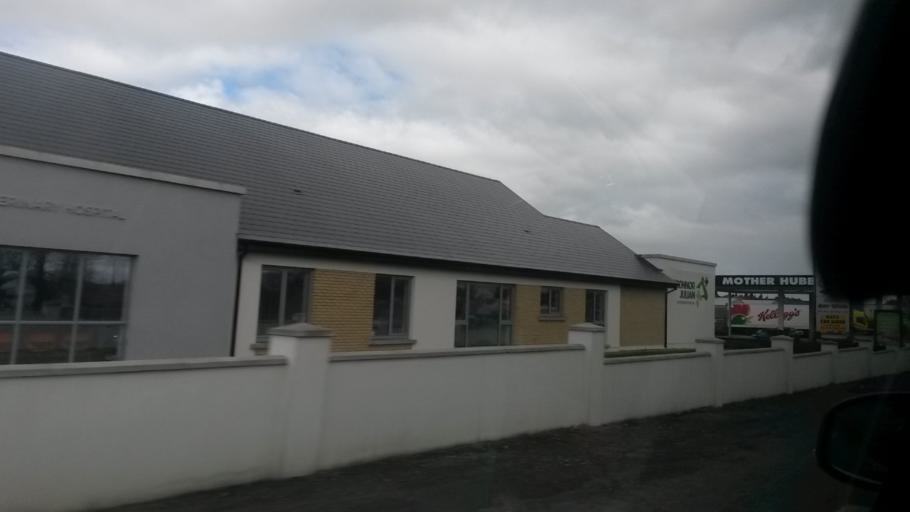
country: IE
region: Munster
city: Cashel
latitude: 52.5063
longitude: -7.8911
